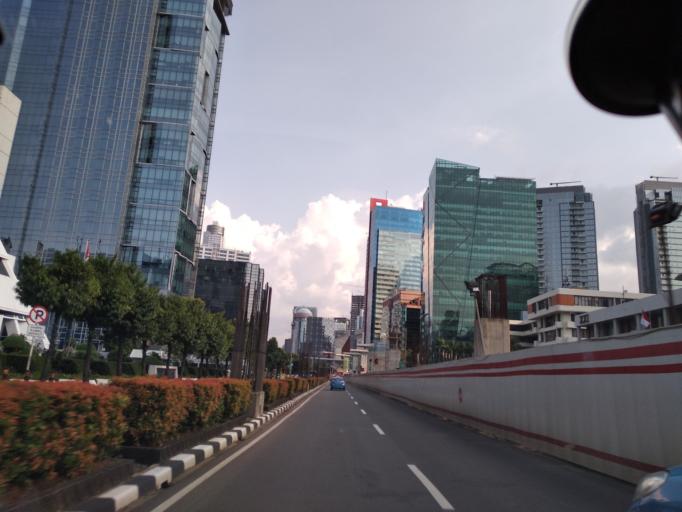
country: ID
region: Jakarta Raya
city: Jakarta
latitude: -6.2148
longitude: 106.8307
